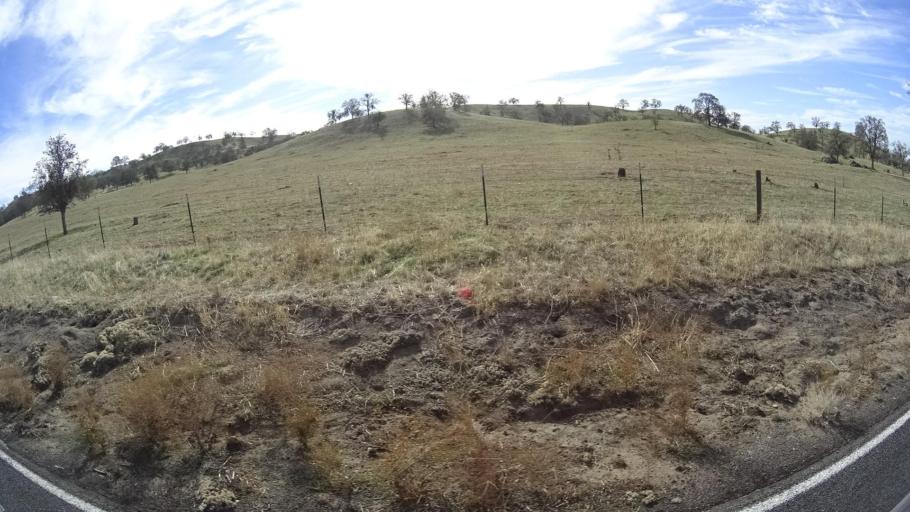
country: US
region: California
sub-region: Kern County
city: Oildale
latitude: 35.6274
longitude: -118.8374
